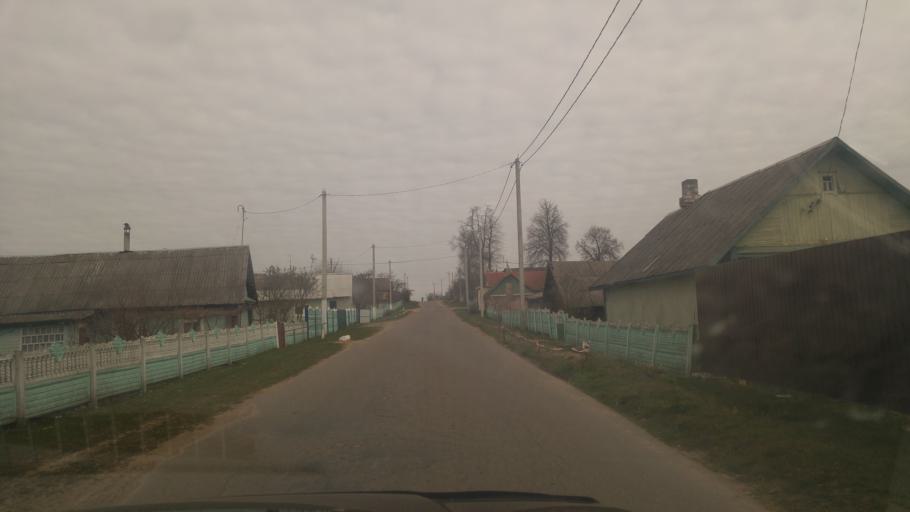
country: BY
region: Minsk
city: Blon'
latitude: 53.5263
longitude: 28.1646
